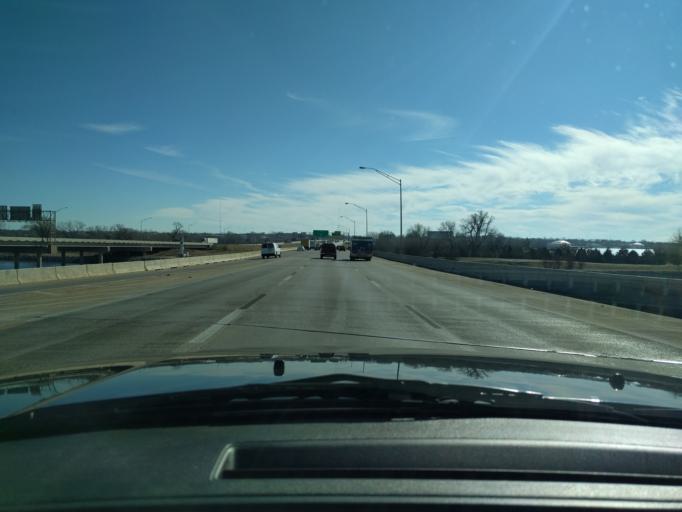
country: US
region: Oklahoma
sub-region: Oklahoma County
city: Oklahoma City
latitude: 35.4596
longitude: -97.4930
